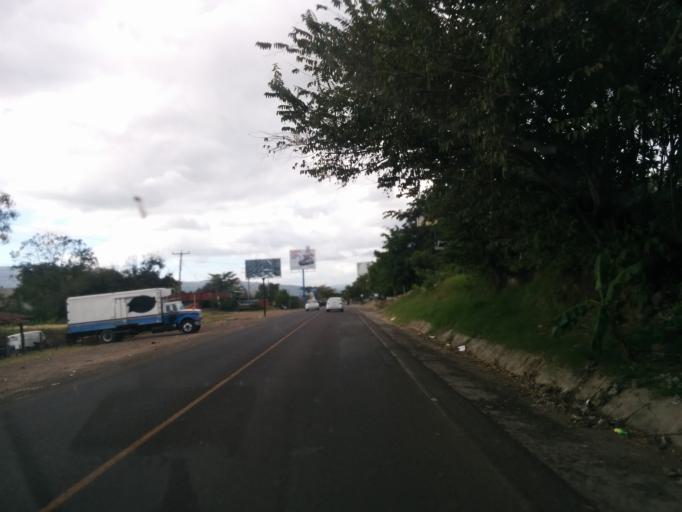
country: NI
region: Esteli
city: Esteli
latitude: 13.0627
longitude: -86.3460
